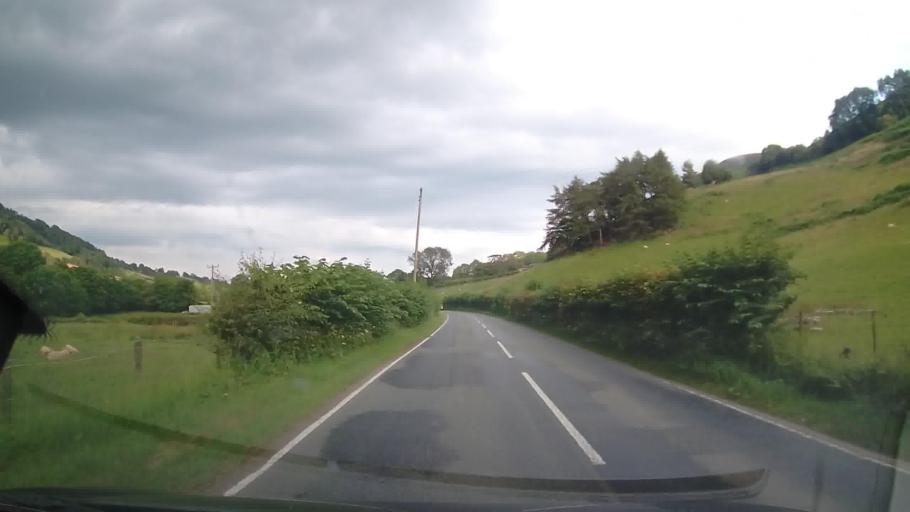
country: GB
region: Wales
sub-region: Sir Powys
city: Llangynog
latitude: 52.8226
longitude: -3.3885
